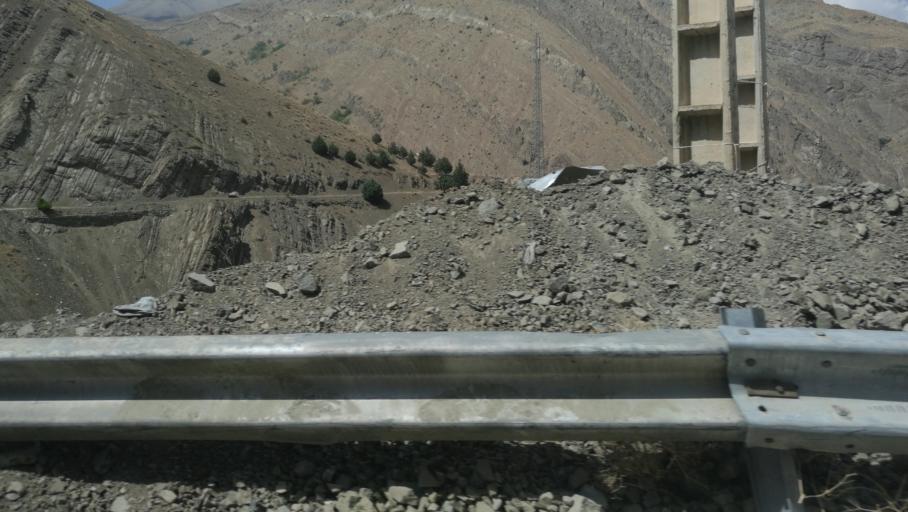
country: IR
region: Alborz
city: Karaj
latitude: 35.9772
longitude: 51.0950
